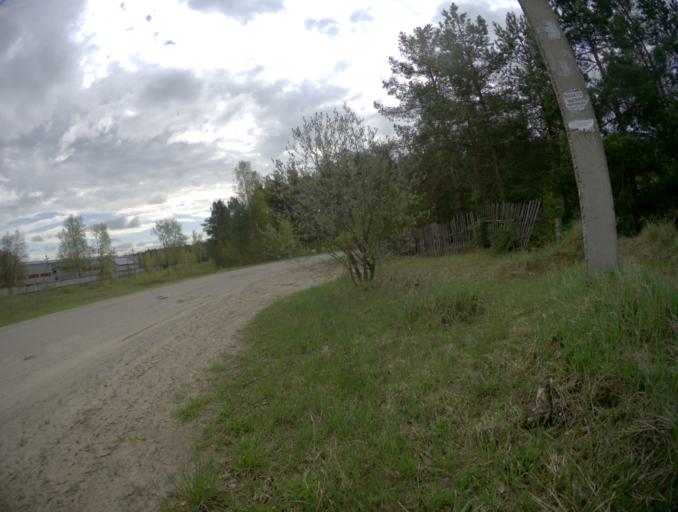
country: RU
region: Vladimir
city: Golovino
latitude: 55.9465
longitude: 40.4444
